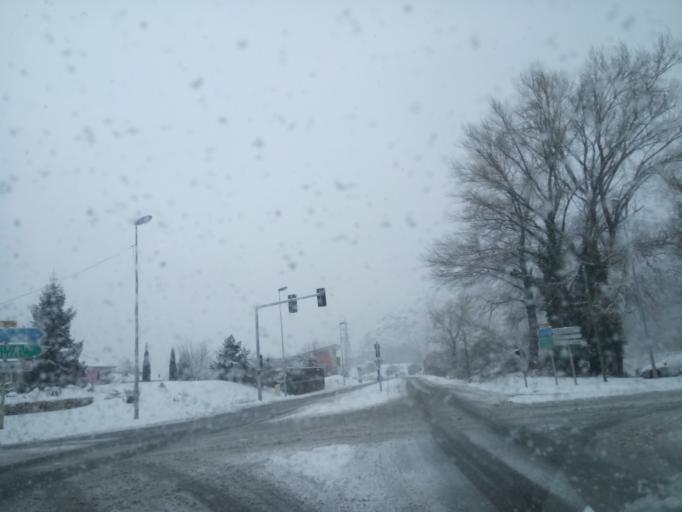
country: FR
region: Rhone-Alpes
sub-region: Departement de la Savoie
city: Villargondran
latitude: 45.2757
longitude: 6.3596
